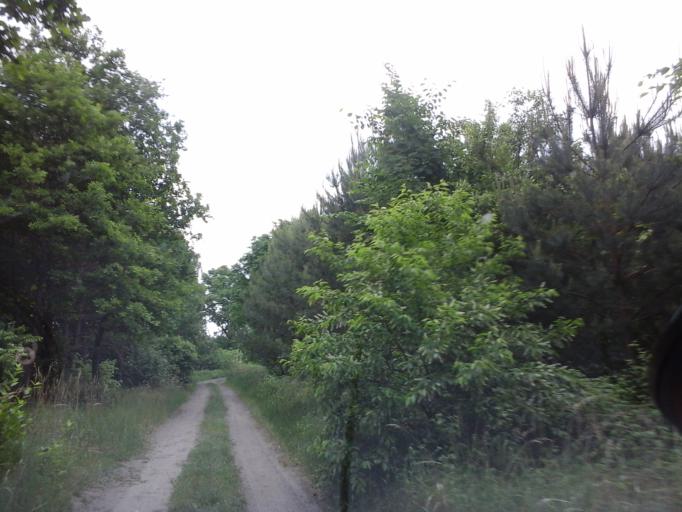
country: PL
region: West Pomeranian Voivodeship
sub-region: Powiat choszczenski
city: Recz
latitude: 53.1459
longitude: 15.5991
